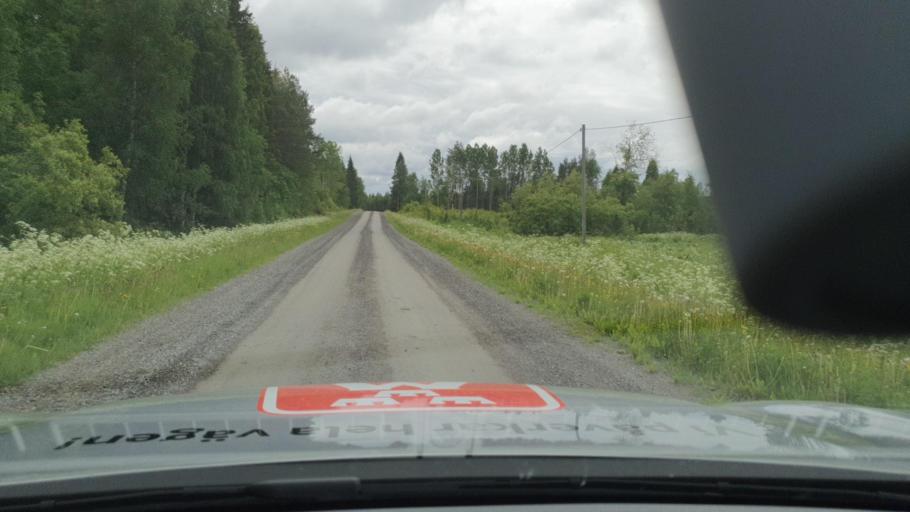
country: SE
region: Norrbotten
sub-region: Lulea Kommun
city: Ranea
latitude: 65.9587
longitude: 22.0744
